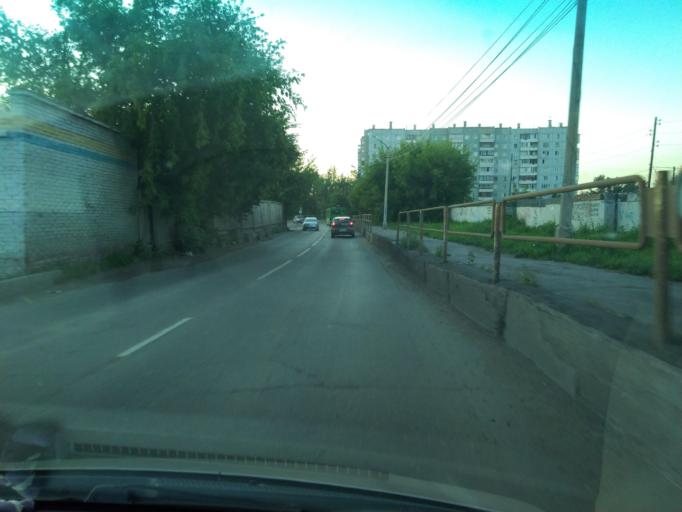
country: RU
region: Krasnoyarskiy
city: Krasnoyarsk
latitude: 55.9847
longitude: 92.8717
